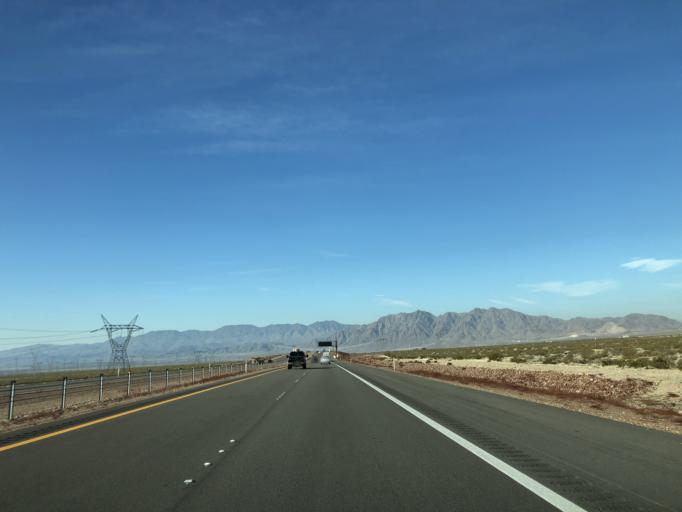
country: US
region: Nevada
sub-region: Clark County
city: Boulder City
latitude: 35.9346
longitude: -114.8342
